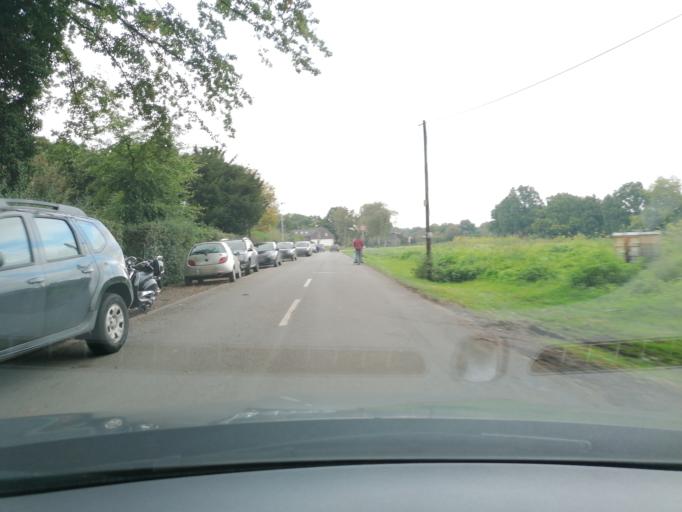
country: DE
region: North Rhine-Westphalia
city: Herten
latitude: 51.5727
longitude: 7.1005
